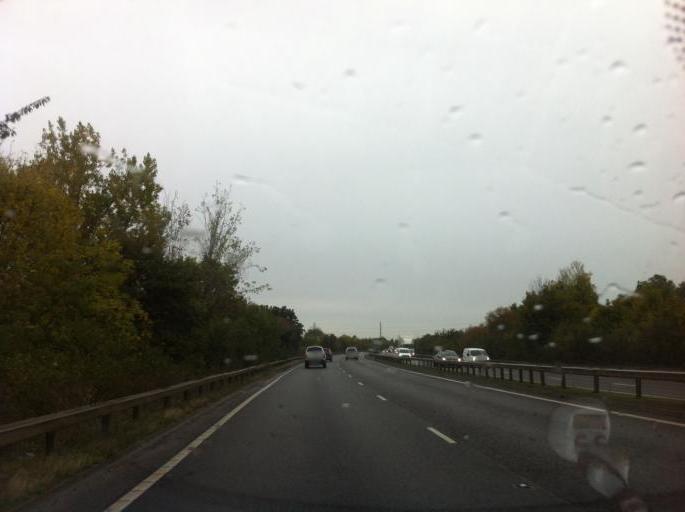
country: GB
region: England
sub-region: Peterborough
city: Peterborough
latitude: 52.5609
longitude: -0.2335
